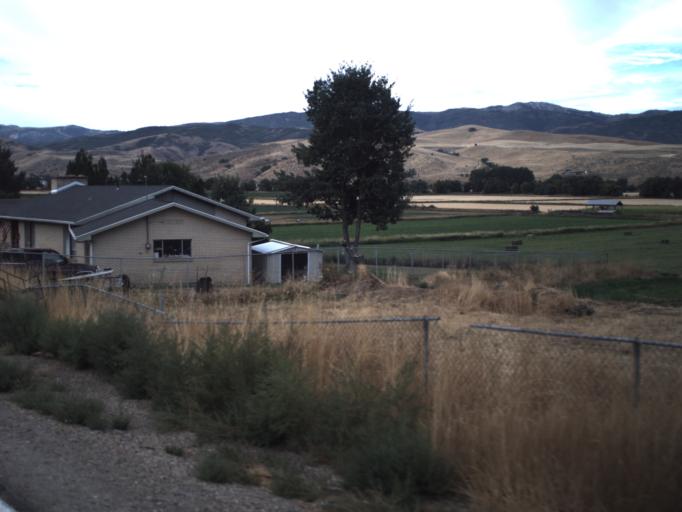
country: US
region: Utah
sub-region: Morgan County
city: Morgan
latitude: 41.0280
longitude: -111.6749
